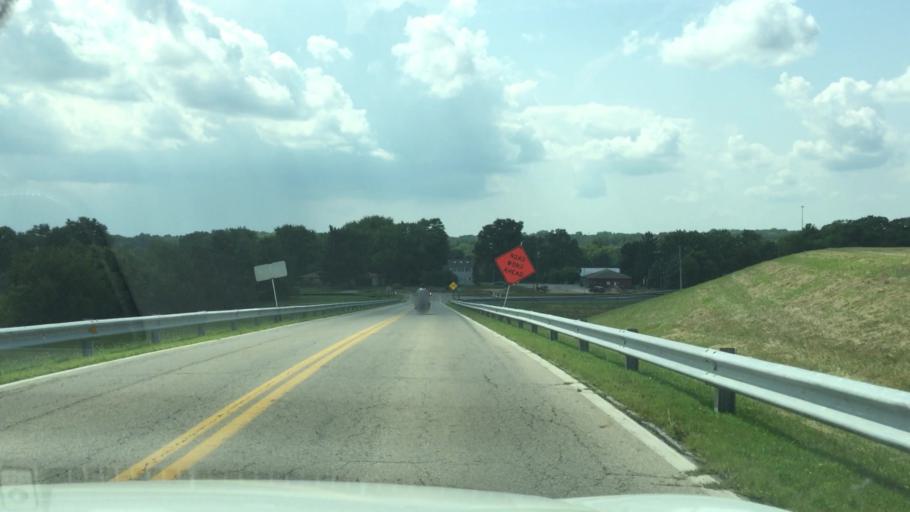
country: US
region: Ohio
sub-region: Clark County
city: Northridge
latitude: 39.9472
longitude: -83.7456
